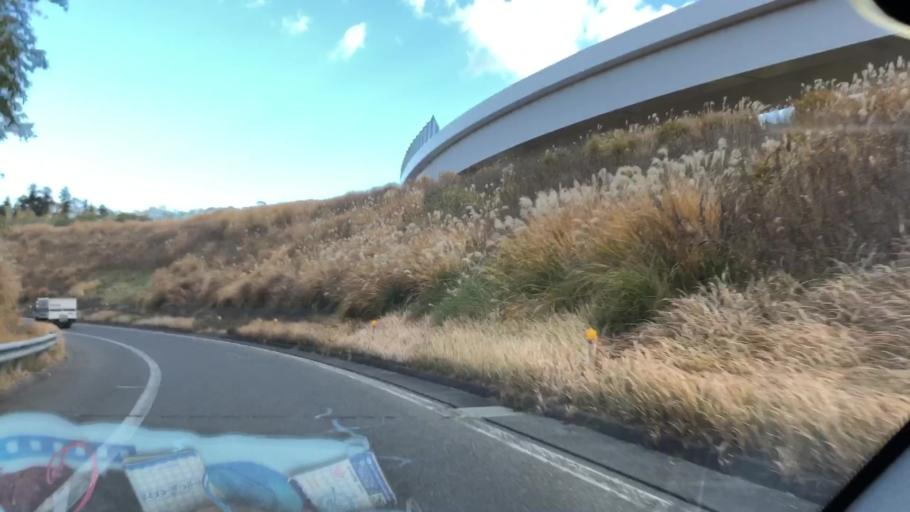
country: JP
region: Chiba
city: Kisarazu
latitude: 35.3763
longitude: 139.9790
